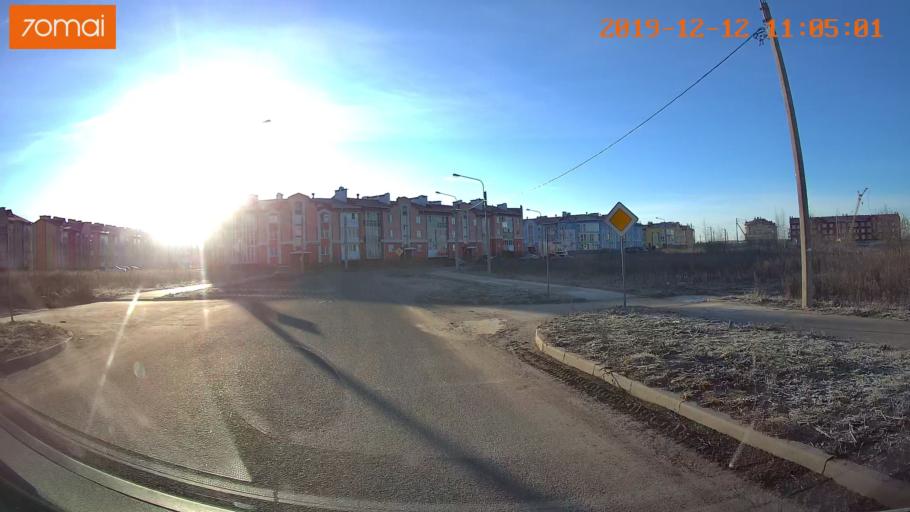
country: RU
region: Ivanovo
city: Kokhma
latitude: 56.9511
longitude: 41.1024
